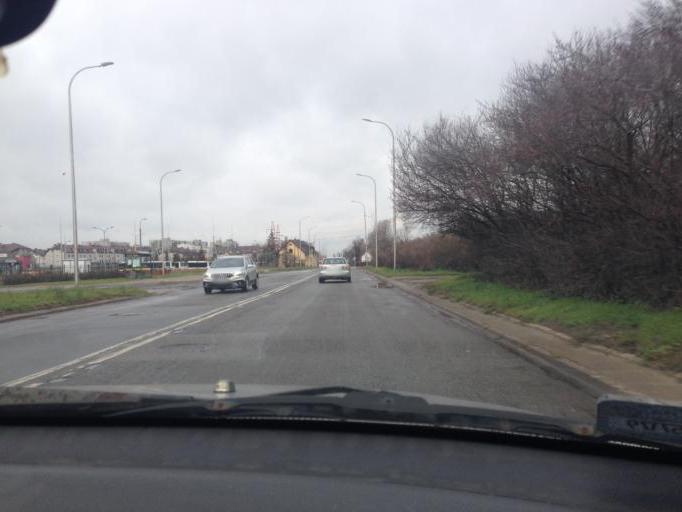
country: PL
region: Opole Voivodeship
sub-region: Powiat opolski
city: Opole
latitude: 50.6773
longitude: 17.9589
